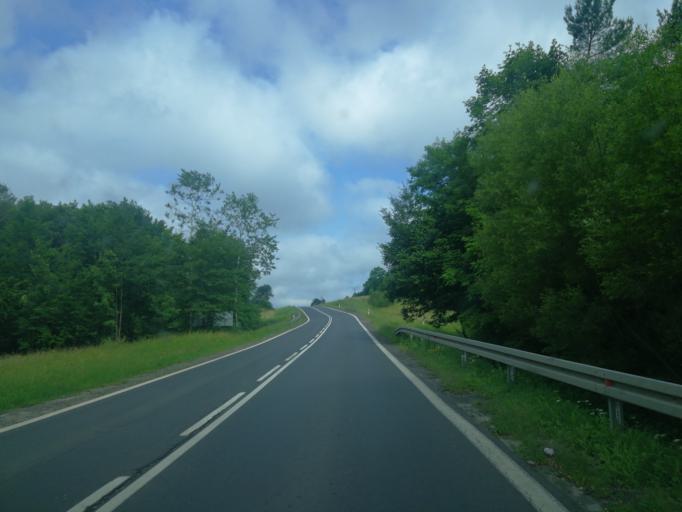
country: PL
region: Subcarpathian Voivodeship
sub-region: Powiat leski
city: Uherce Mineralne
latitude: 49.4671
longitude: 22.3849
